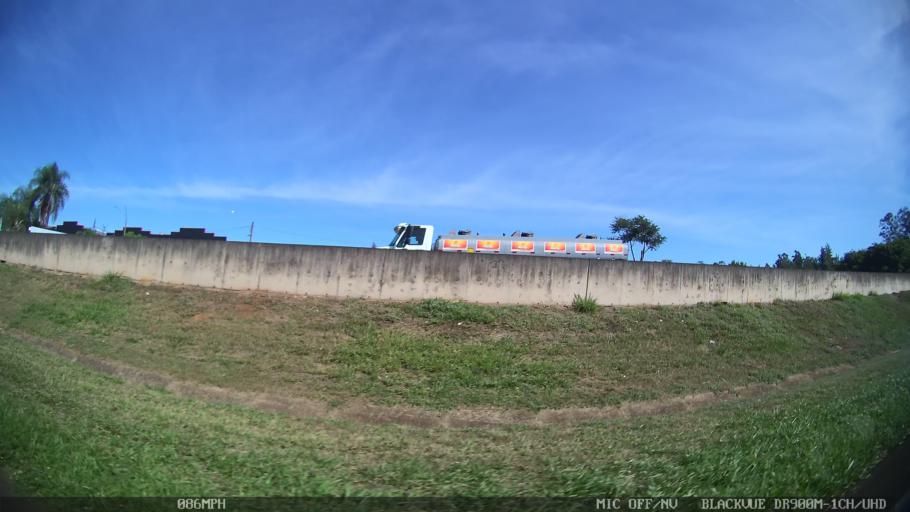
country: BR
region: Sao Paulo
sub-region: Pirassununga
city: Pirassununga
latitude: -21.9945
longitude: -47.4469
